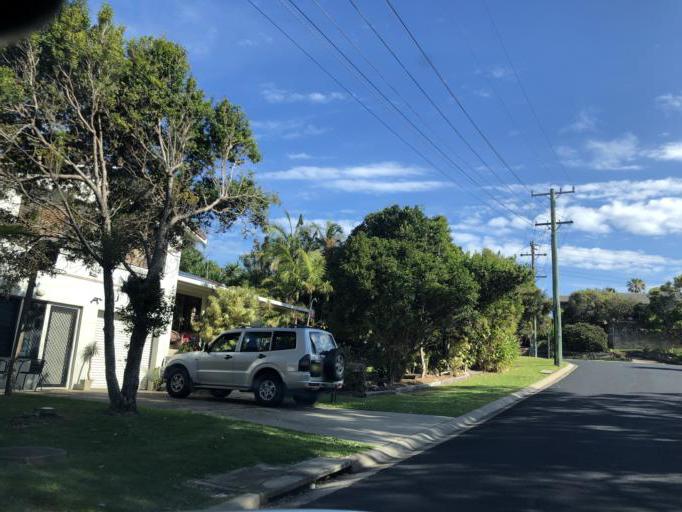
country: AU
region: New South Wales
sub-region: Coffs Harbour
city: Moonee Beach
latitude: -30.2327
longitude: 153.1513
